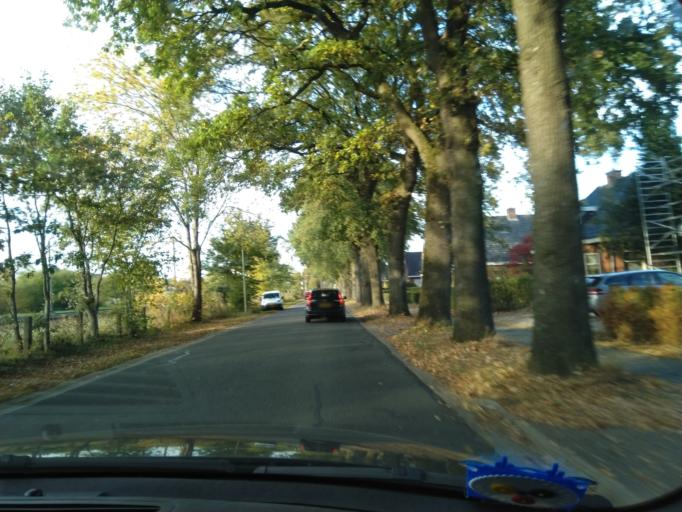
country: NL
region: Drenthe
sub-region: Gemeente Tynaarlo
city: Tynaarlo
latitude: 53.0779
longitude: 6.6284
